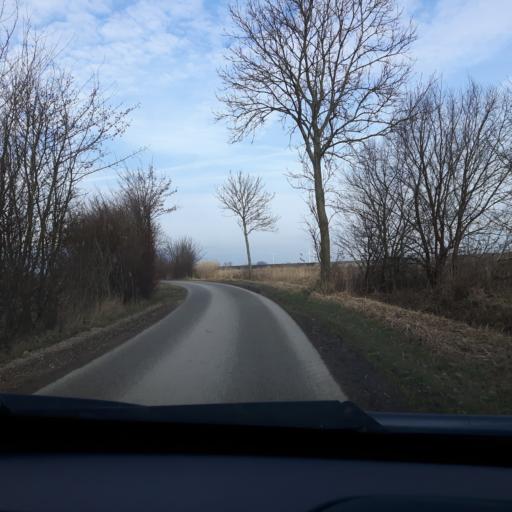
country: NL
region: Zeeland
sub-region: Gemeente Goes
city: Goes
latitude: 51.4284
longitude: 3.9167
